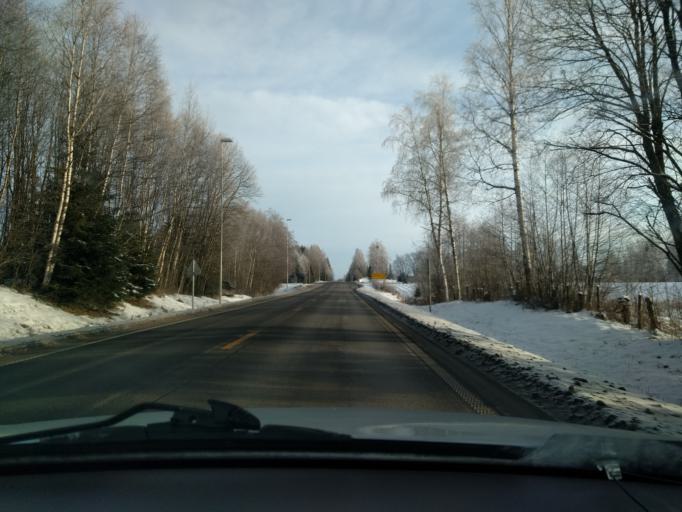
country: NO
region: Hedmark
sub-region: Elverum
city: Elverum
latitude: 60.9186
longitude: 11.6537
